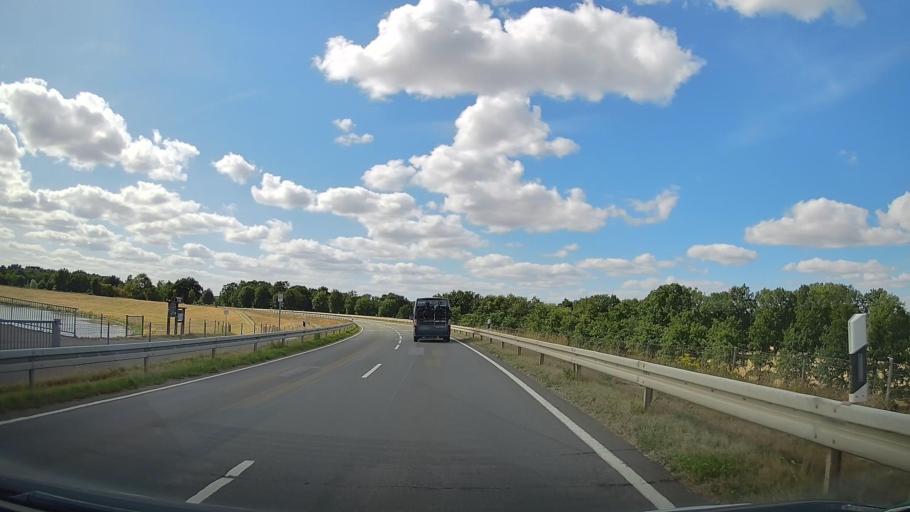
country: DE
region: Lower Saxony
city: Alfhausen
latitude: 52.4978
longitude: 7.9815
